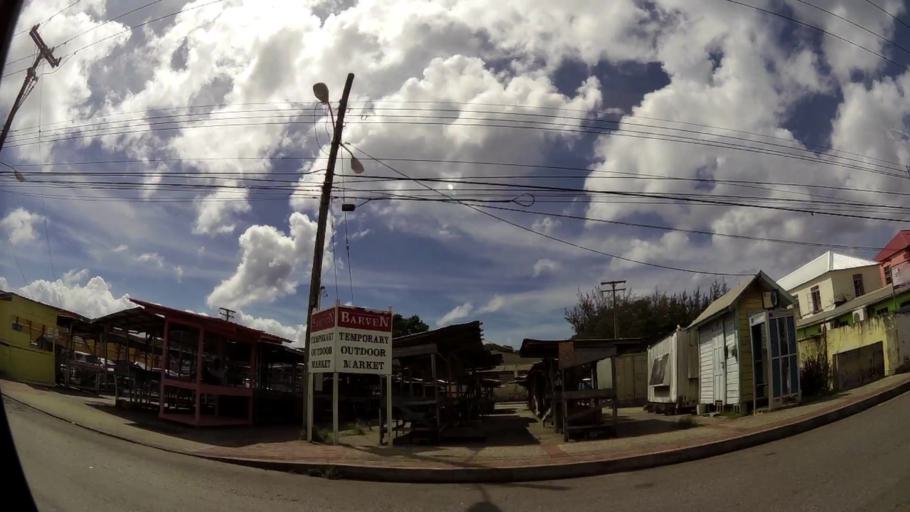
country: BB
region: Saint Michael
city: Bridgetown
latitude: 13.0992
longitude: -59.6221
